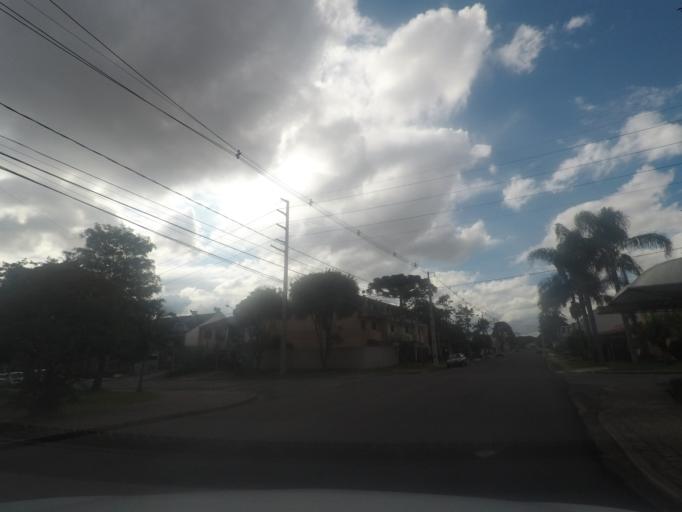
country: BR
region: Parana
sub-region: Pinhais
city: Pinhais
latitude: -25.4614
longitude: -49.2271
